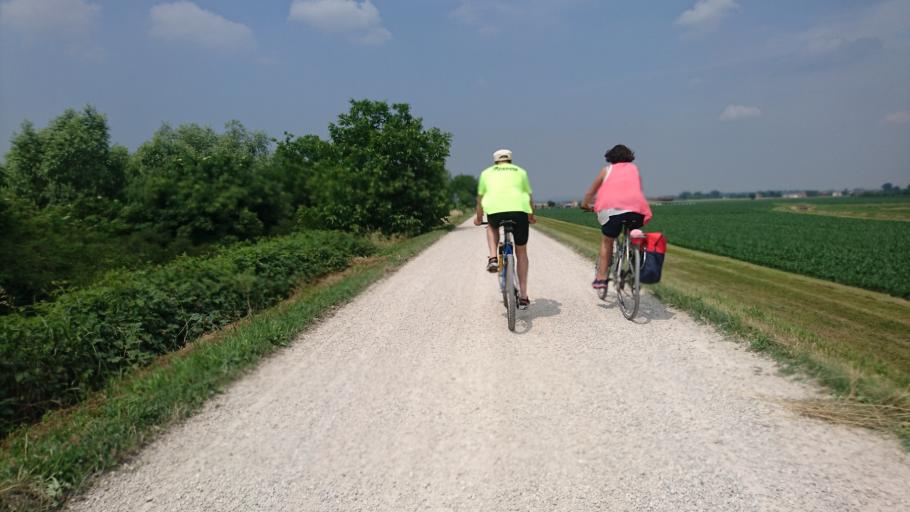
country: IT
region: Veneto
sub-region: Provincia di Padova
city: Bovolenta
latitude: 45.2737
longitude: 11.9208
